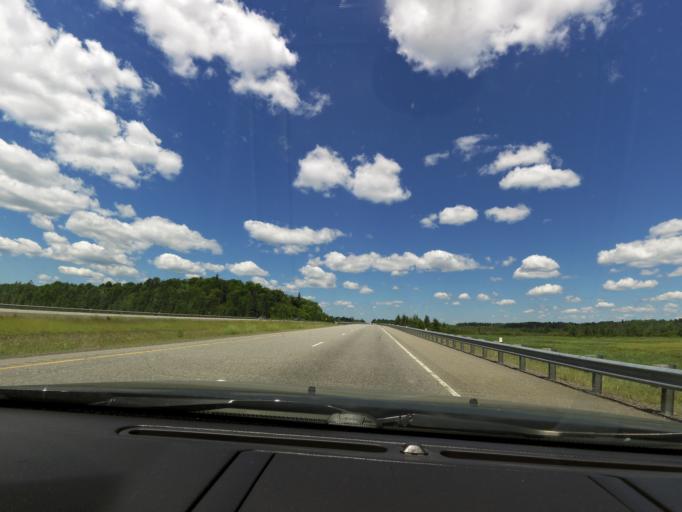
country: CA
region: Ontario
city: Huntsville
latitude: 45.5023
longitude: -79.2980
